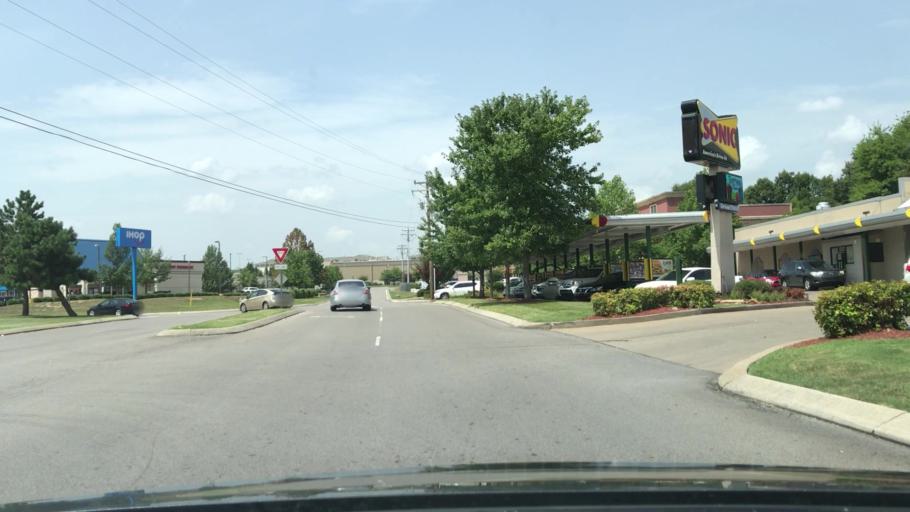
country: US
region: Tennessee
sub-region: Rutherford County
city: La Vergne
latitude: 35.9803
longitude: -86.5620
